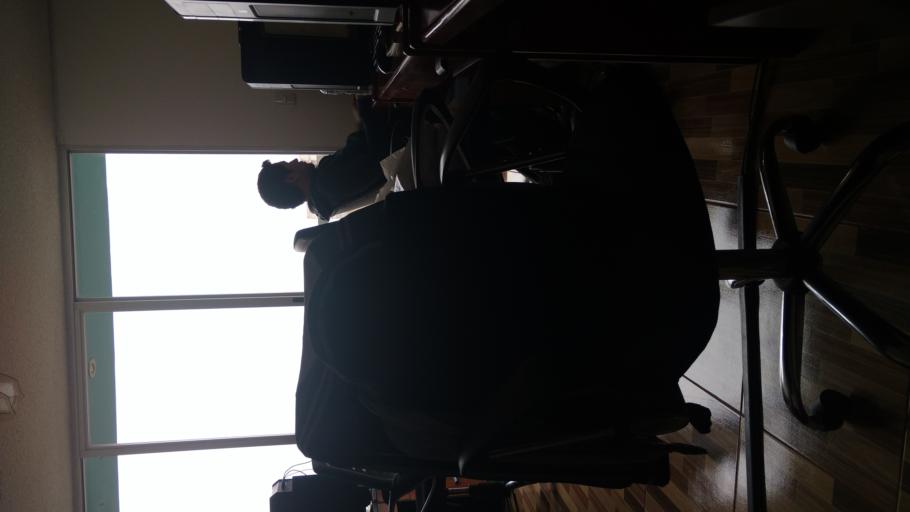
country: PE
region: Lima
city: Lima
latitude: -12.0657
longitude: -77.0545
